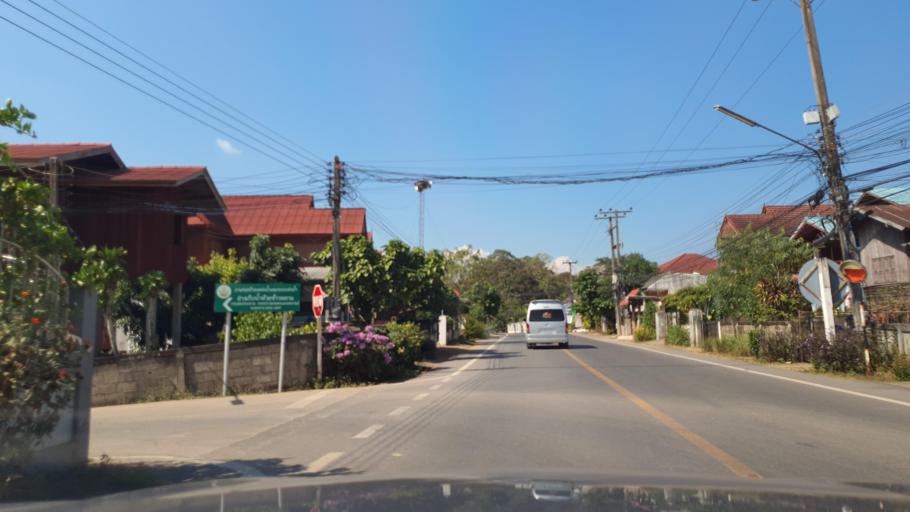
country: TH
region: Nan
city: Tha Wang Pha
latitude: 19.0759
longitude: 100.8666
